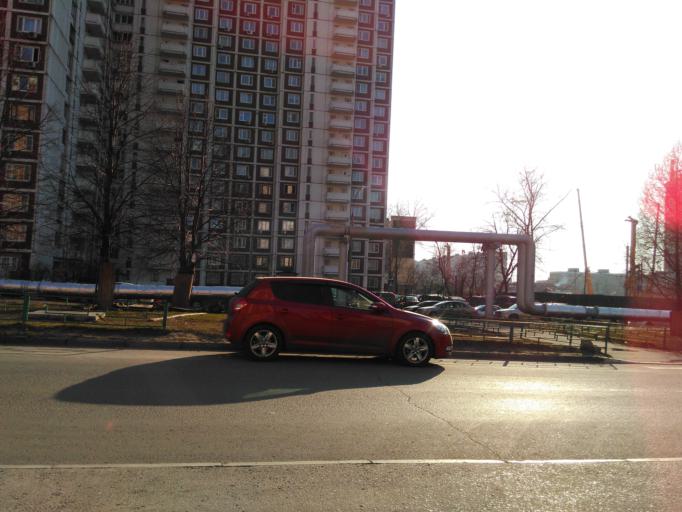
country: RU
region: Moscow
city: Ramenki
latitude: 55.6984
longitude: 37.5024
